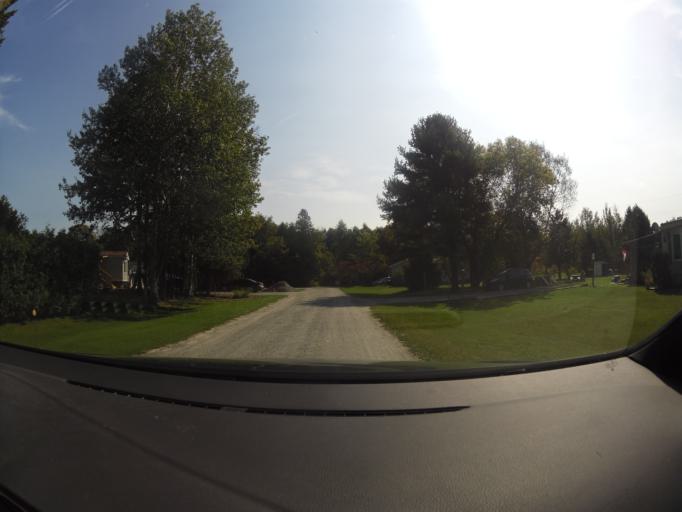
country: CA
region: Ontario
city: Arnprior
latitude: 45.3415
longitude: -76.2080
